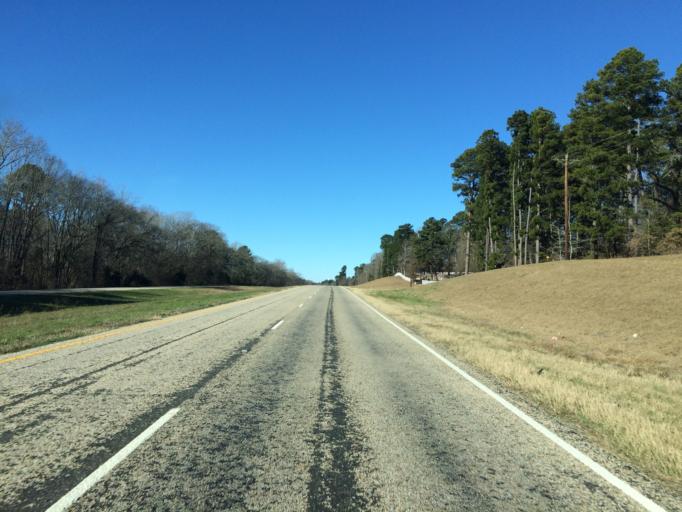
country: US
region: Texas
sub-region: Wood County
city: Mineola
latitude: 32.6460
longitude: -95.4074
